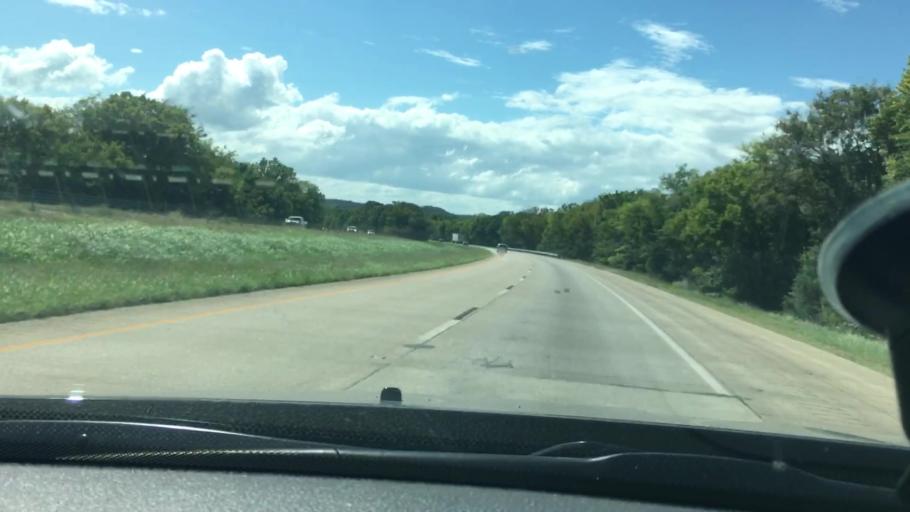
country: US
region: Oklahoma
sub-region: Sequoyah County
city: Vian
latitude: 35.4934
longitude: -95.0055
